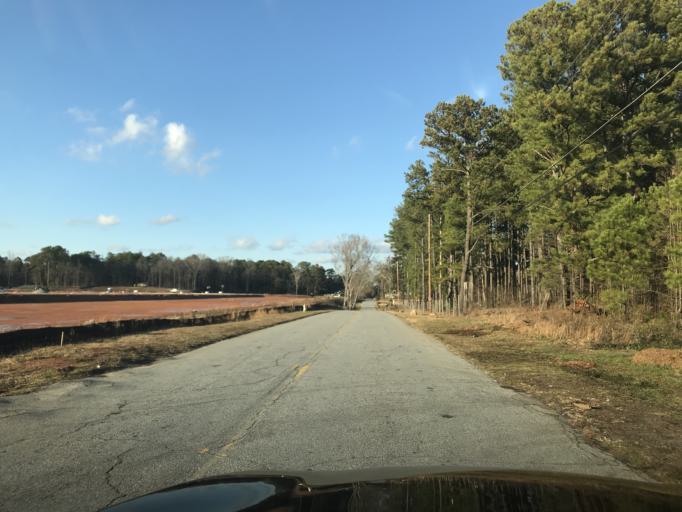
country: US
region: Georgia
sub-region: Fulton County
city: College Park
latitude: 33.6249
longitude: -84.4842
